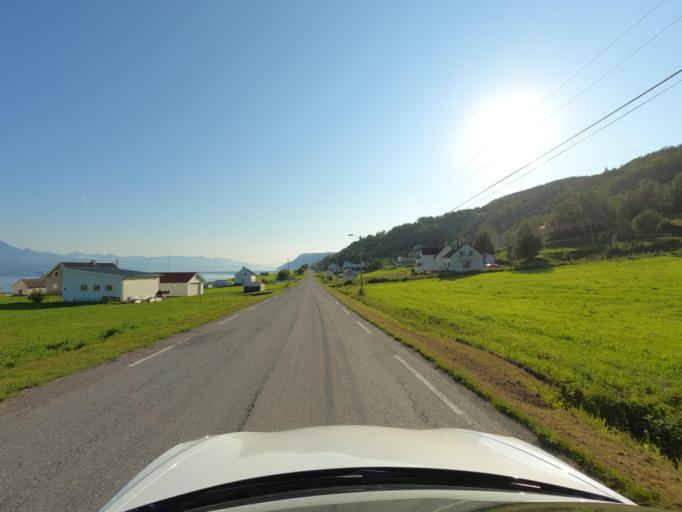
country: NO
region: Nordland
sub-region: Narvik
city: Bjerkvik
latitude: 68.5306
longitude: 17.4691
